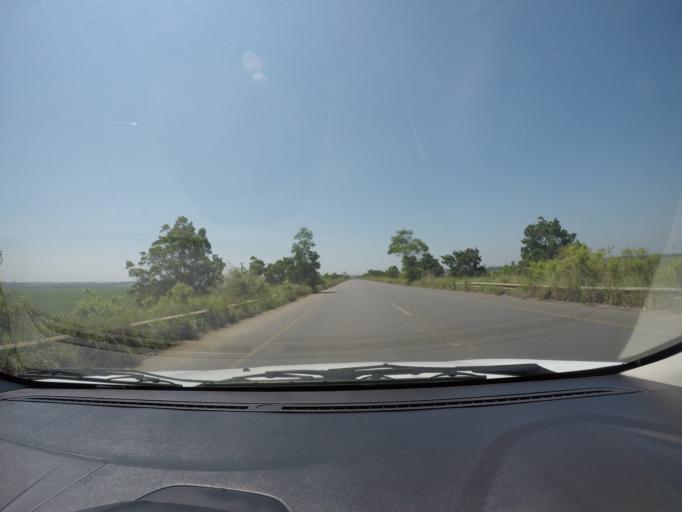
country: ZA
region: KwaZulu-Natal
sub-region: uThungulu District Municipality
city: Empangeni
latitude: -28.7935
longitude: 31.9581
